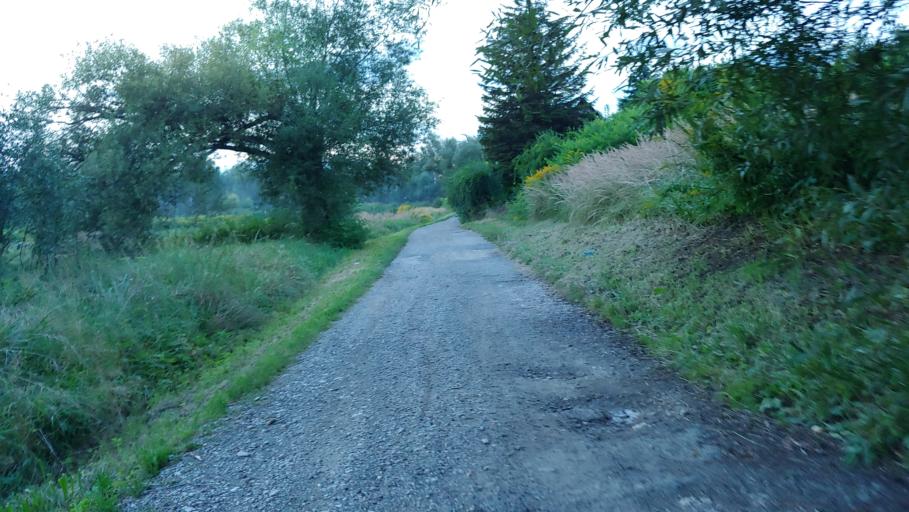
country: PL
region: Lesser Poland Voivodeship
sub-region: Powiat chrzanowski
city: Trzebinia
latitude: 50.1643
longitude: 19.4670
